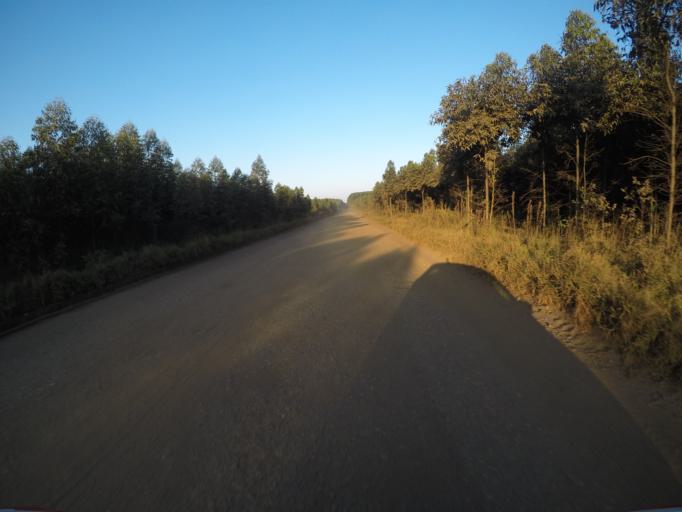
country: ZA
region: KwaZulu-Natal
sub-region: uThungulu District Municipality
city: KwaMbonambi
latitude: -28.6685
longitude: 32.0751
